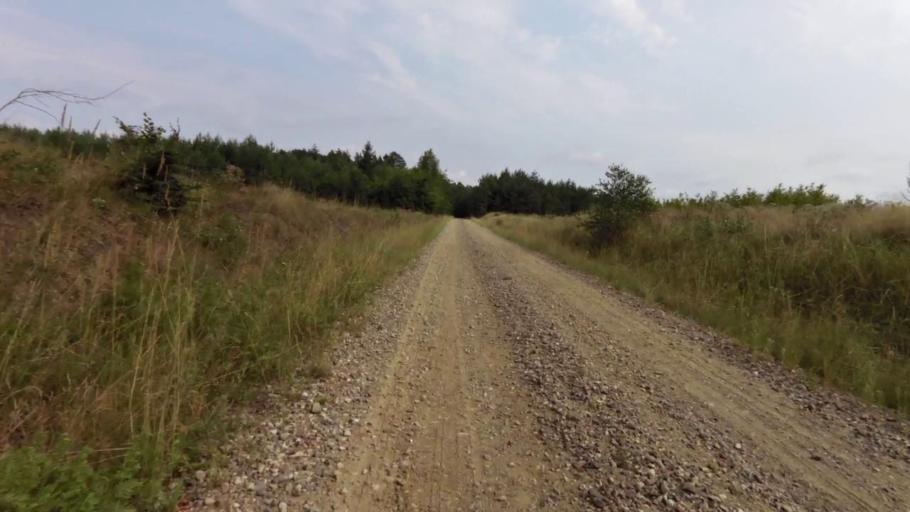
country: PL
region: West Pomeranian Voivodeship
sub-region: Powiat drawski
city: Zlocieniec
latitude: 53.5629
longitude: 15.9193
